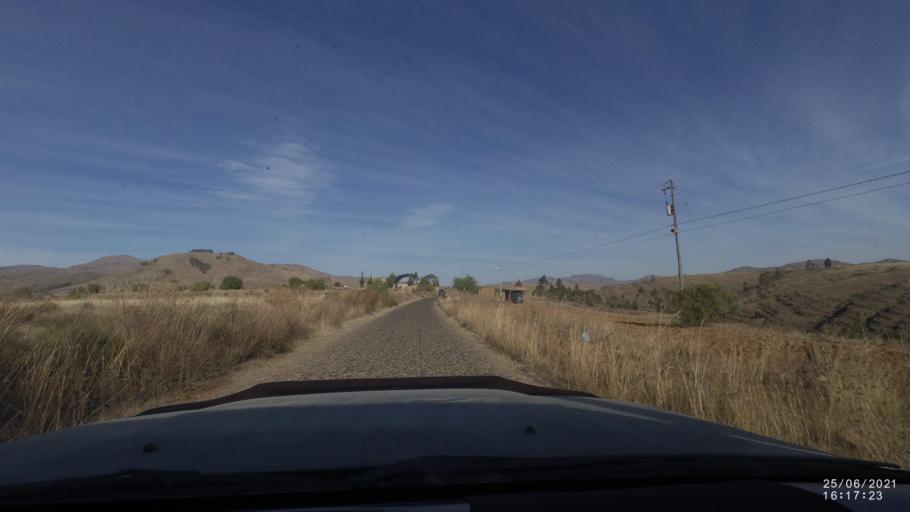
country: BO
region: Cochabamba
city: Cliza
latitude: -17.7264
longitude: -65.8568
